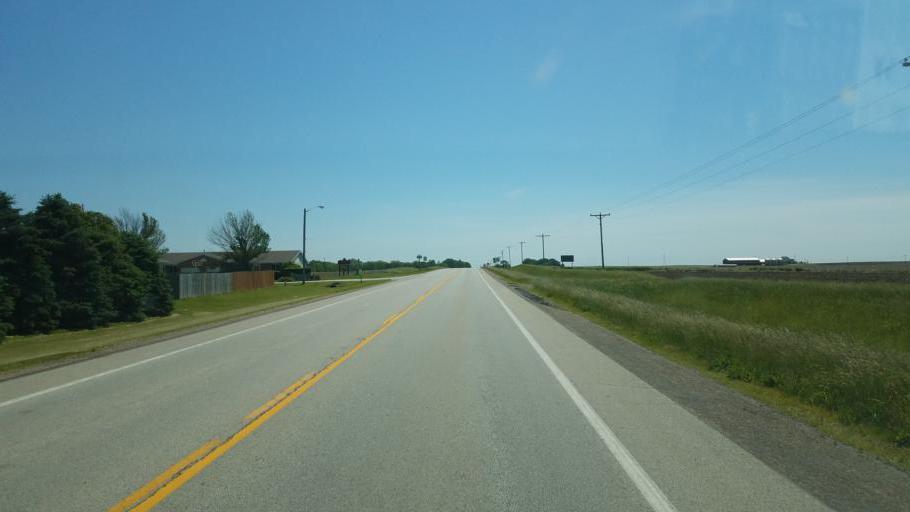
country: US
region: Illinois
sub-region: McLean County
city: Heyworth
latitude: 40.3121
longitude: -88.9658
